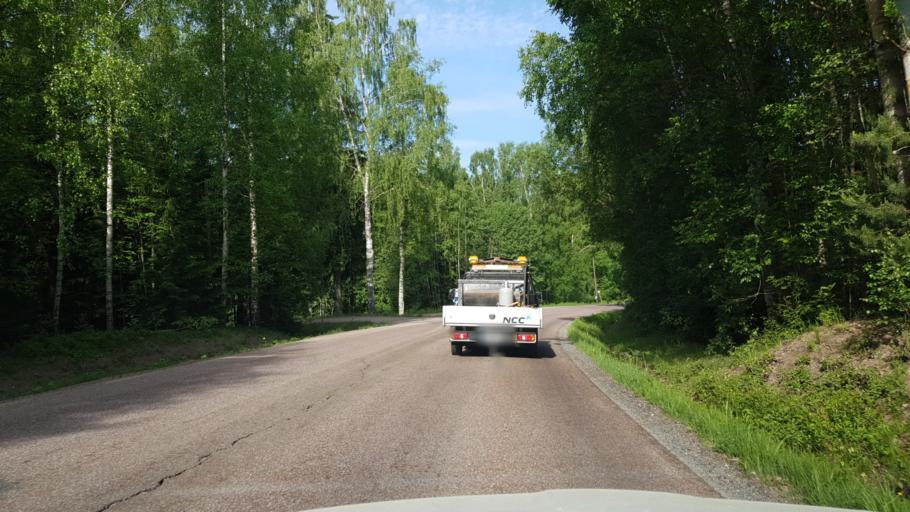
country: SE
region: Dalarna
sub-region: Saters Kommun
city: Saeter
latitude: 60.4136
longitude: 15.6849
